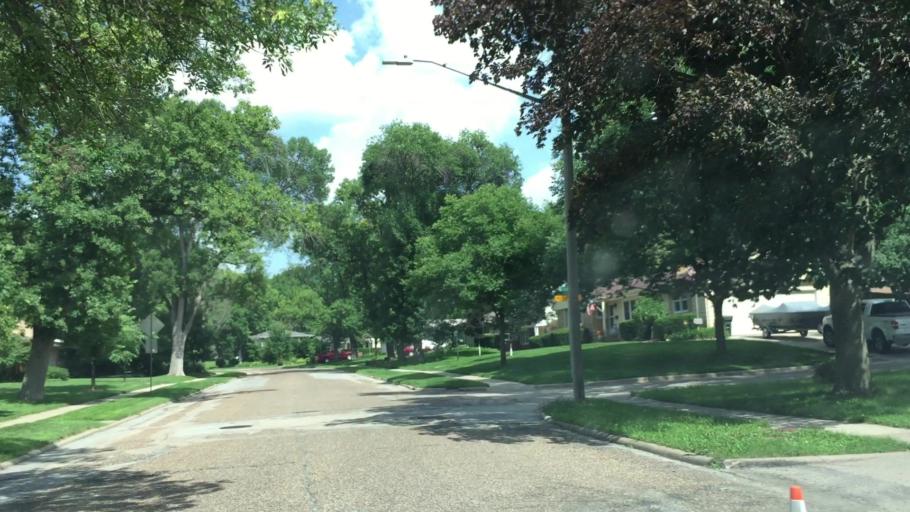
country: US
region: Iowa
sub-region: Johnson County
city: Iowa City
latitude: 41.6609
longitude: -91.5106
